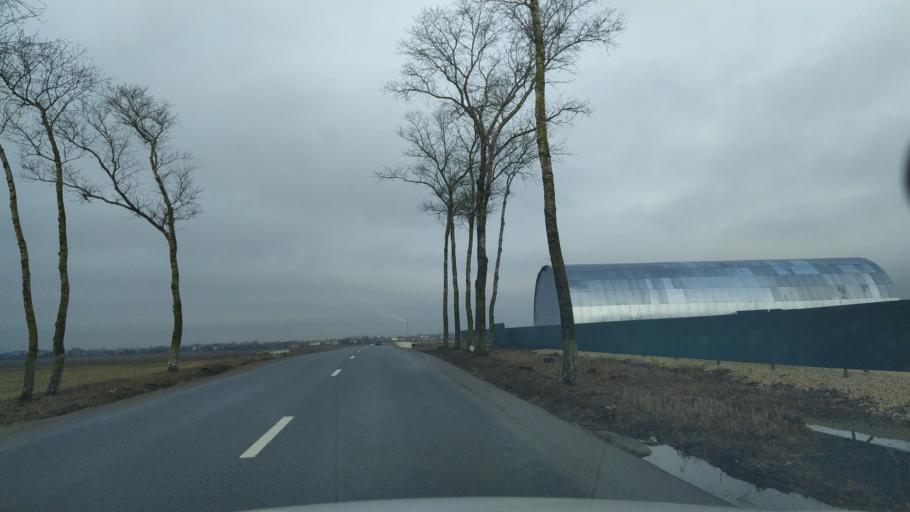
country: RU
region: St.-Petersburg
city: Aleksandrovskaya
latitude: 59.7140
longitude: 30.3339
